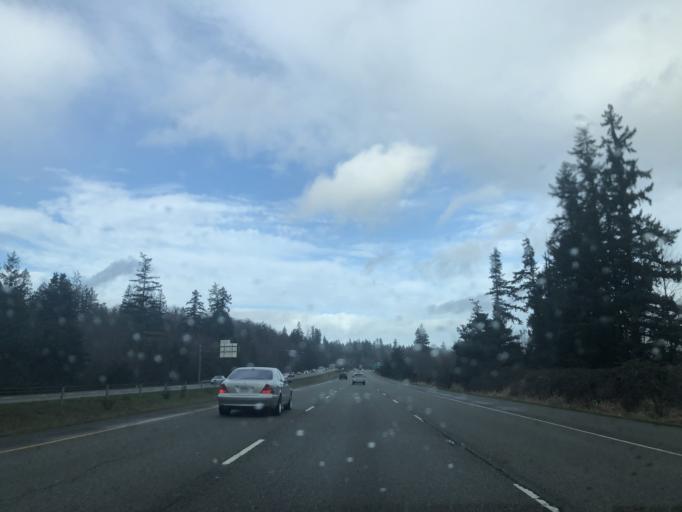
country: US
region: Washington
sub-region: Kitsap County
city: Silverdale
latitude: 47.6705
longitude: -122.6887
